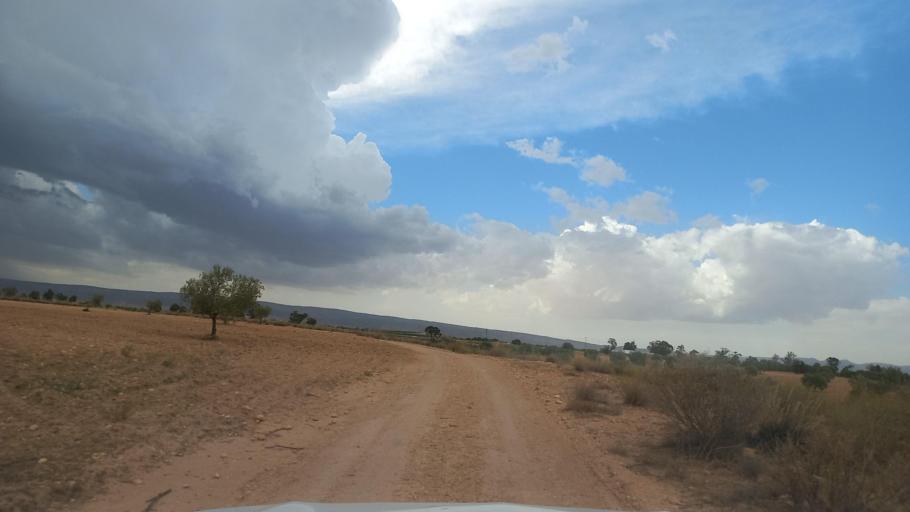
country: TN
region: Al Qasrayn
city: Kasserine
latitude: 35.2456
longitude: 9.0065
